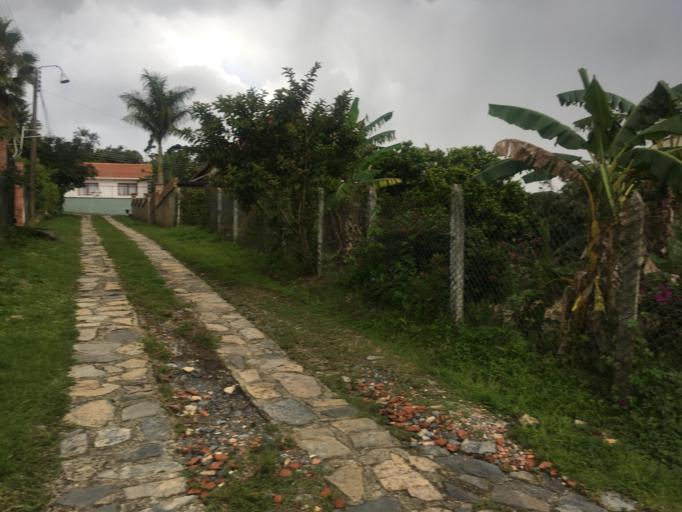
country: CO
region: Santander
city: Barbosa
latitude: 5.9179
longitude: -73.6036
